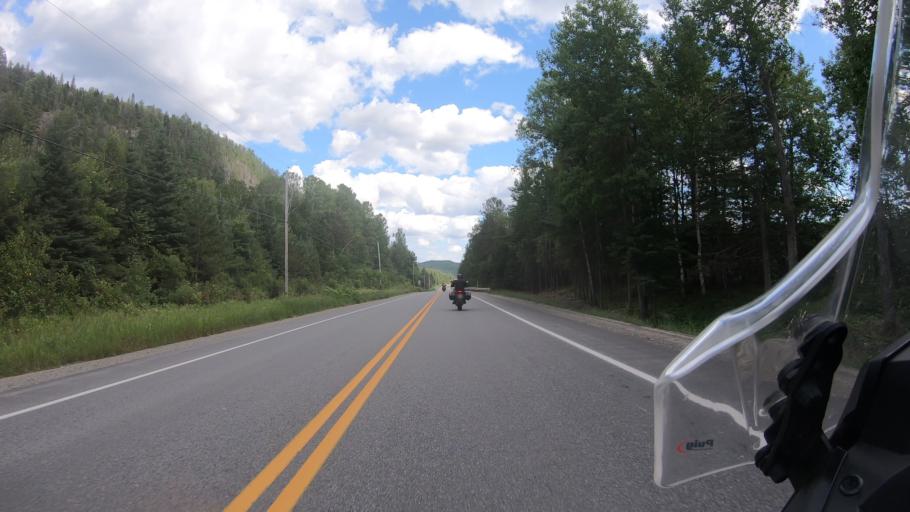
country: CA
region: Quebec
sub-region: Mauricie
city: Saint-Tite
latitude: 46.9920
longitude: -72.9147
